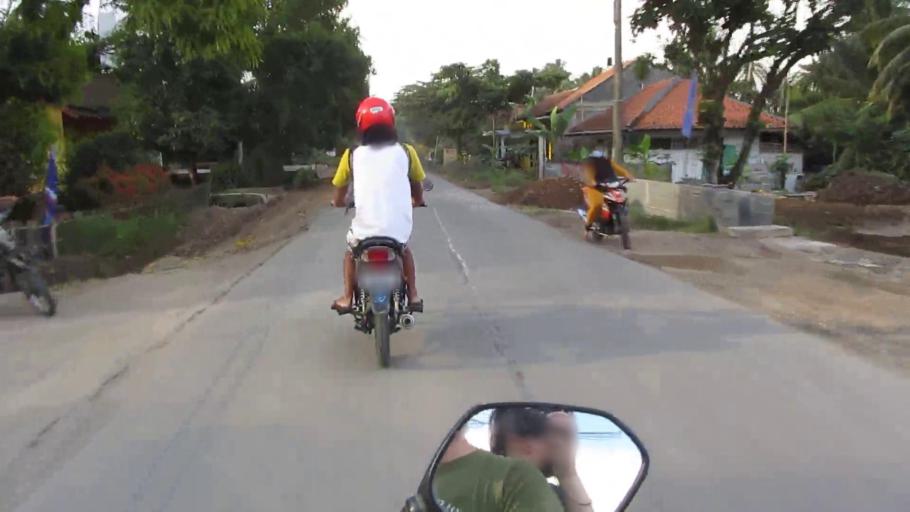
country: ID
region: West Java
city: Balengbeng
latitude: -7.7079
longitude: 108.4918
